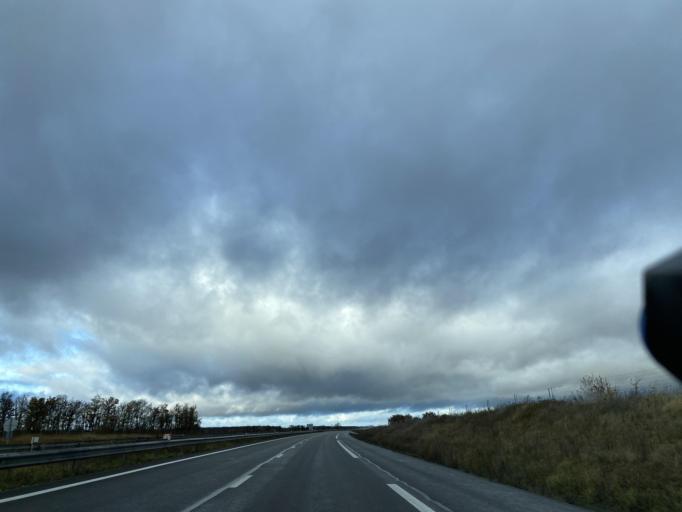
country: FR
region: Centre
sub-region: Departement du Cher
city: Plaimpied-Givaudins
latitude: 46.9855
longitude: 2.4135
